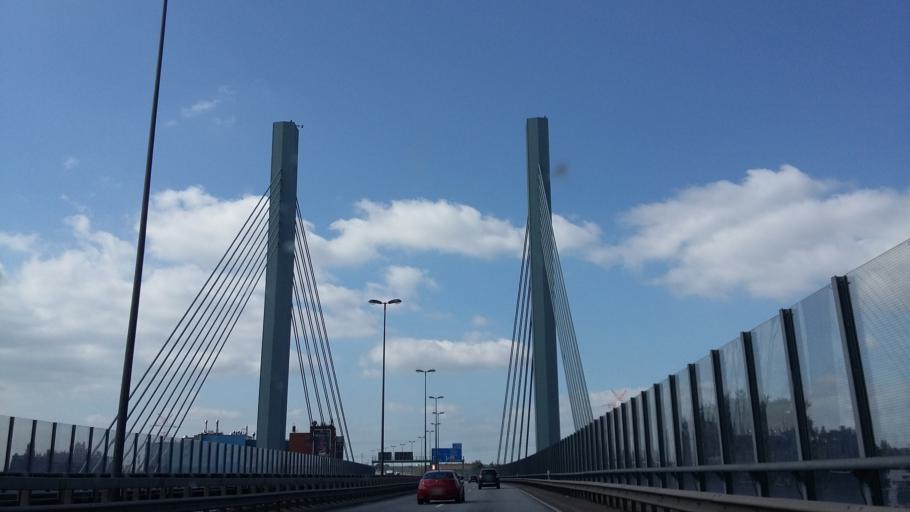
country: DE
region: Bremen
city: Bremen
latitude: 53.0599
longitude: 8.7864
